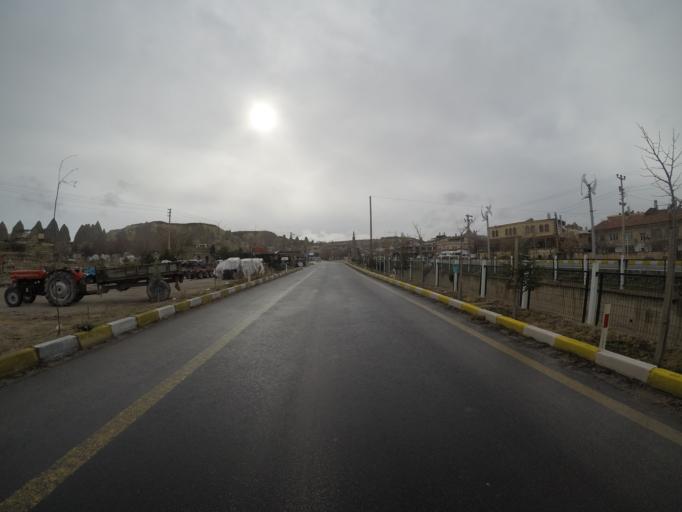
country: TR
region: Nevsehir
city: Goereme
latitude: 38.6469
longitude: 34.8336
